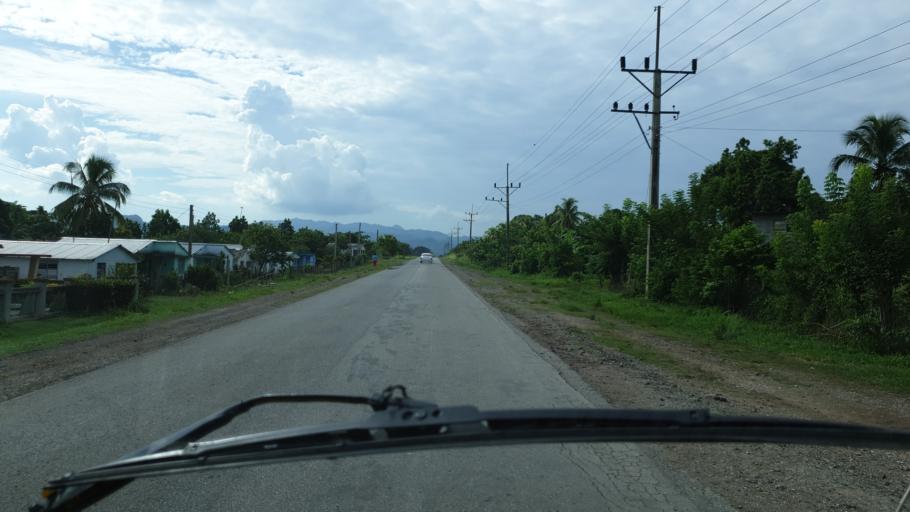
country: CU
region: Cienfuegos
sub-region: Municipio de Cienfuegos
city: Cumanayagua
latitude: 22.0740
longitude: -80.3096
